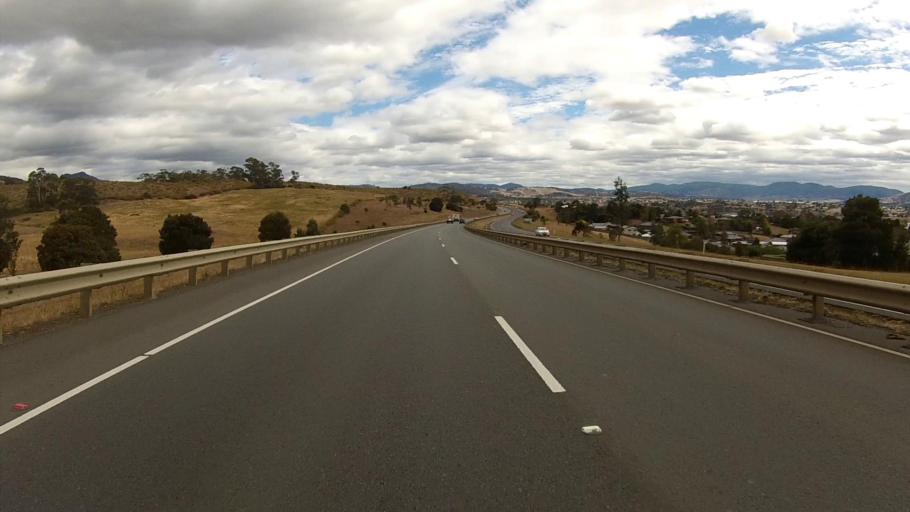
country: AU
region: Tasmania
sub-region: Glenorchy
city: Austins Ferry
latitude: -42.7687
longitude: 147.2366
